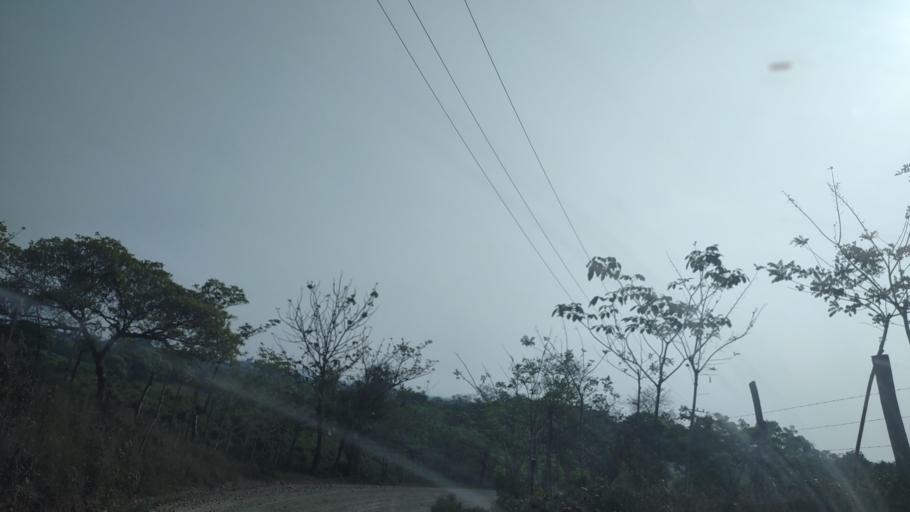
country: MX
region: Tabasco
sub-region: Huimanguillo
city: Francisco Rueda
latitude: 17.6440
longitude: -93.9090
